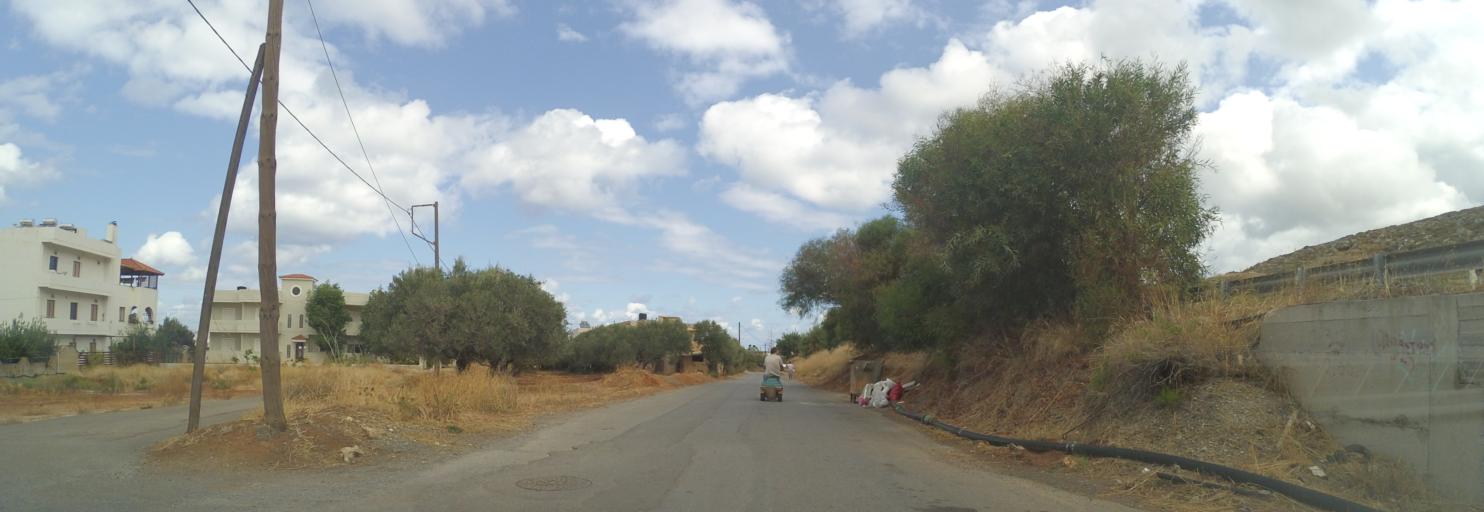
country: GR
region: Crete
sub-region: Nomos Irakleiou
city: Kokkini Hani
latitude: 35.3270
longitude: 25.2618
